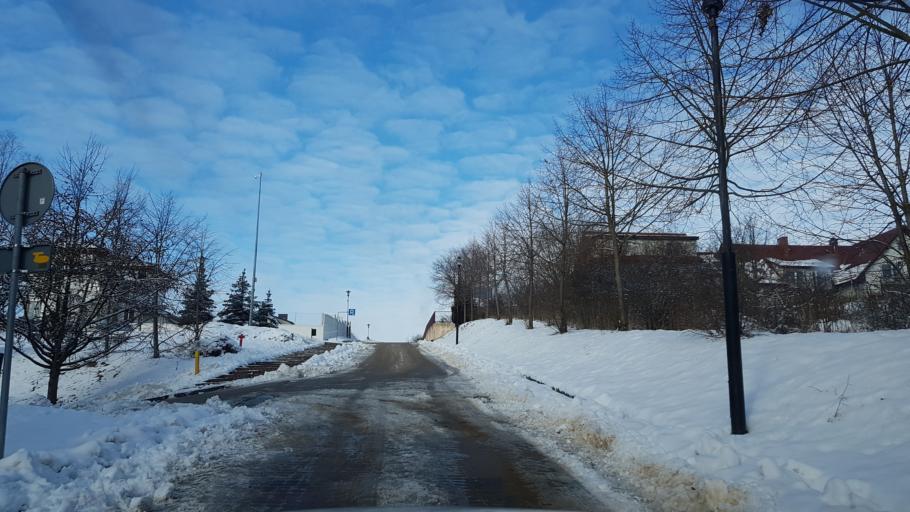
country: PL
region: West Pomeranian Voivodeship
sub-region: Powiat drawski
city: Drawsko Pomorskie
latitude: 53.5162
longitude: 15.8225
